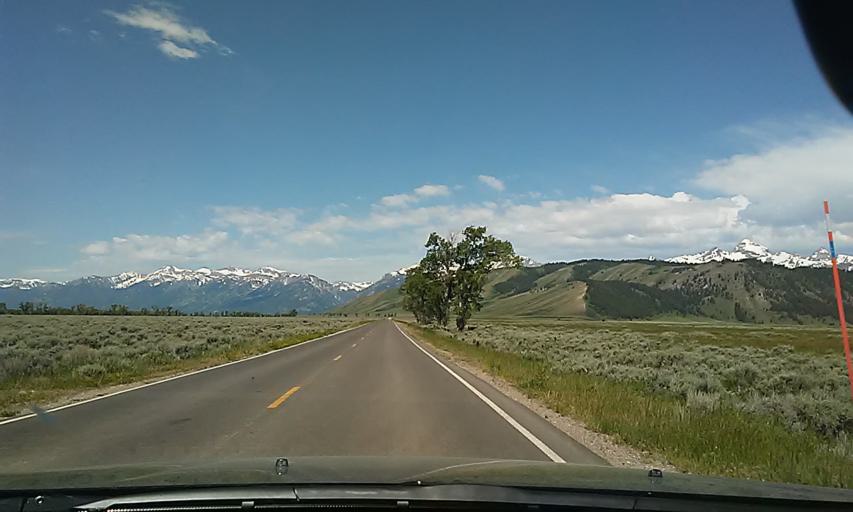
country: US
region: Wyoming
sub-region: Teton County
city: Jackson
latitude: 43.6251
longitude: -110.6389
